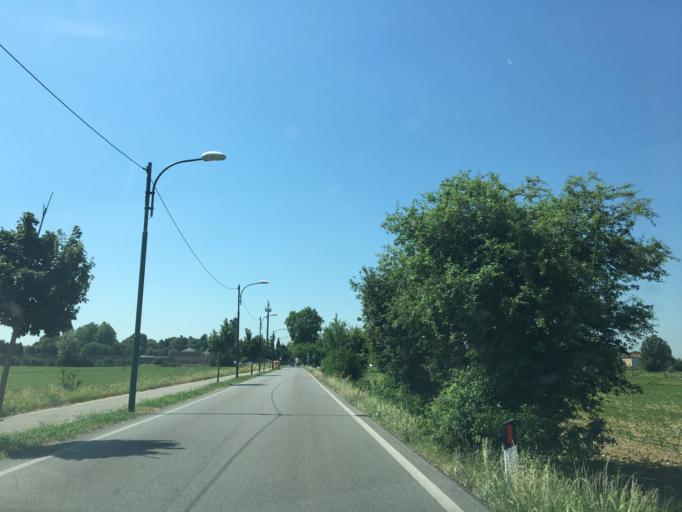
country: IT
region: Veneto
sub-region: Provincia di Venezia
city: Spinea-Orgnano
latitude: 45.4899
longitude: 12.1902
